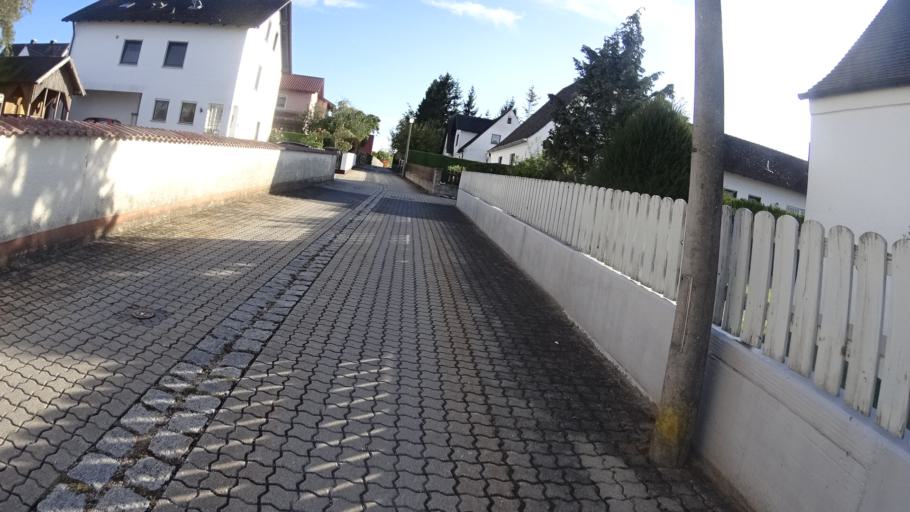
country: DE
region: Bavaria
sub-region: Upper Bavaria
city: Bohmfeld
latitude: 48.8623
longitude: 11.3621
